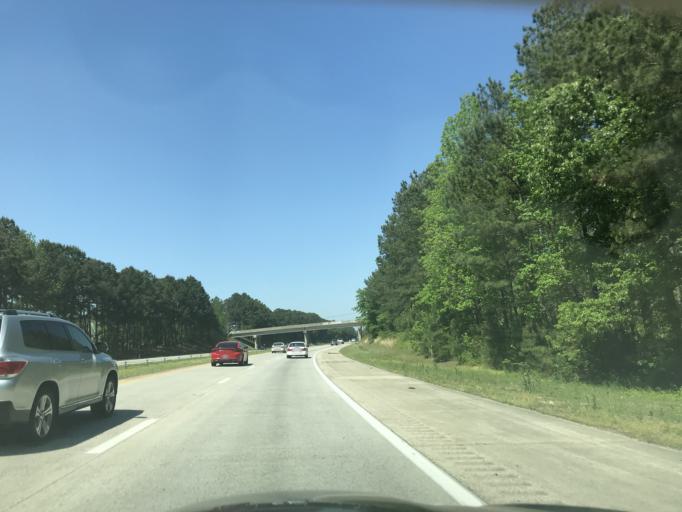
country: US
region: North Carolina
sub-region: Johnston County
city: Clayton
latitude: 35.5508
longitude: -78.5799
